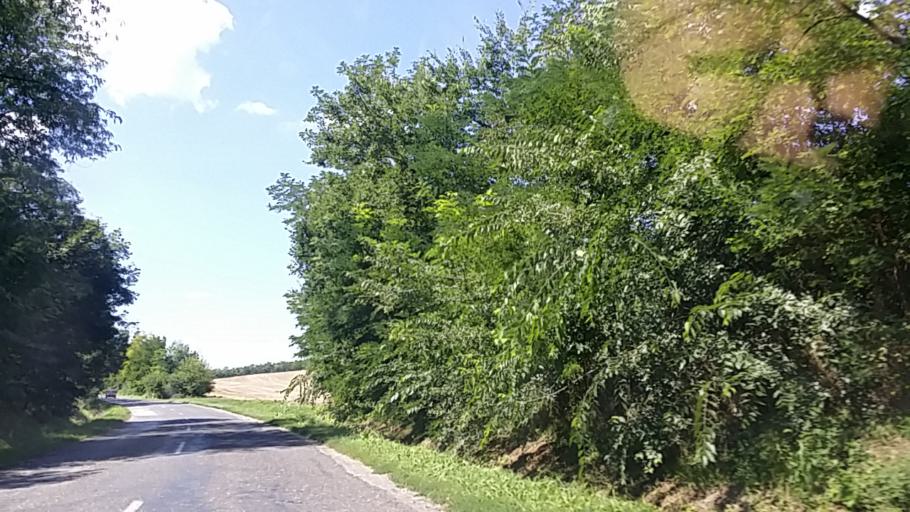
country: HU
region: Fejer
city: Mezoszilas
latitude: 46.7534
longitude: 18.4815
